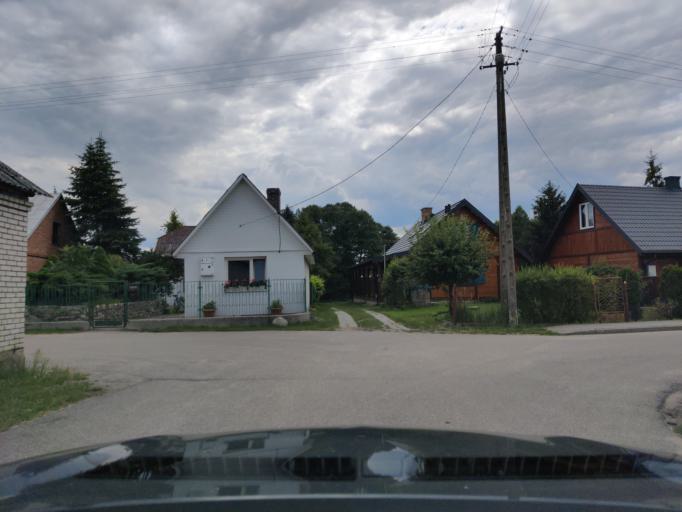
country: PL
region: Masovian Voivodeship
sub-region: Powiat pultuski
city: Pultusk
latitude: 52.7260
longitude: 21.1239
